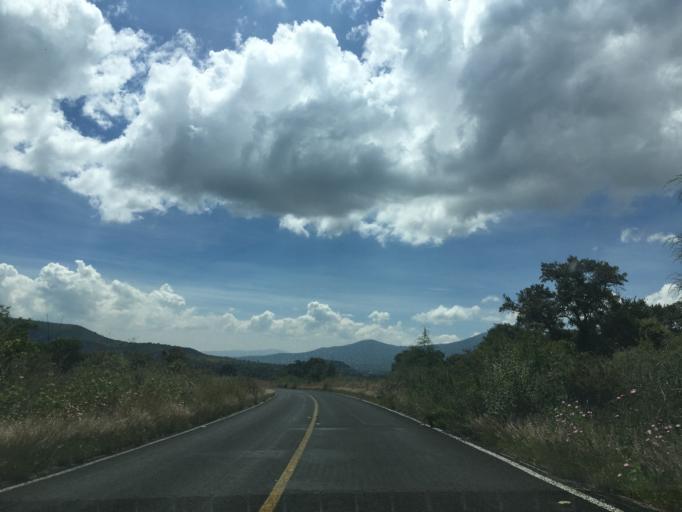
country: MX
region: Michoacan
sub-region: Morelia
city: Cuto de la Esperanza
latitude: 19.7362
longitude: -101.3509
